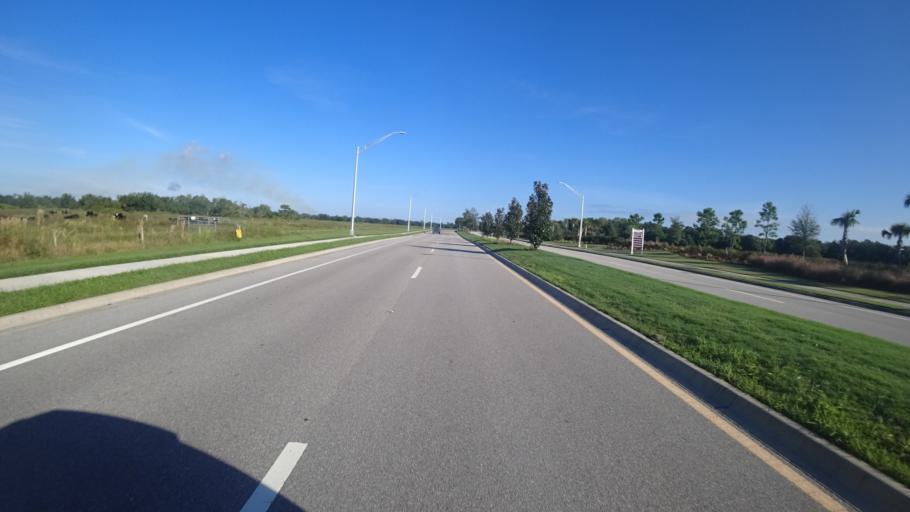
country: US
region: Florida
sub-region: Sarasota County
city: The Meadows
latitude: 27.4328
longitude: -82.3732
